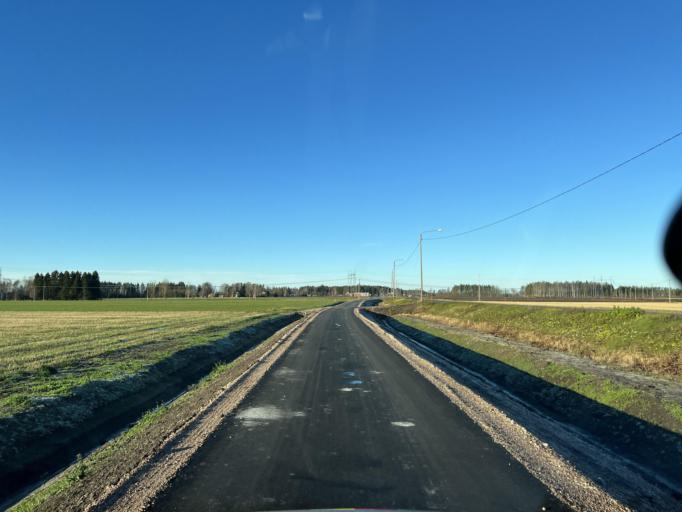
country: FI
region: Northern Ostrobothnia
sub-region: Nivala-Haapajaervi
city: Nivala
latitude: 63.9513
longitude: 24.8790
